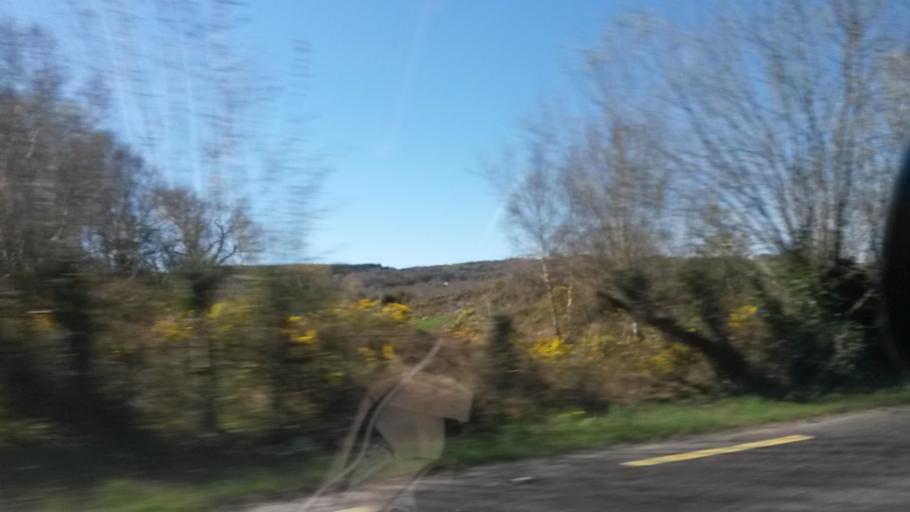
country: IE
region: Munster
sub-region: County Cork
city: Macroom
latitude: 51.9106
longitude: -9.0464
